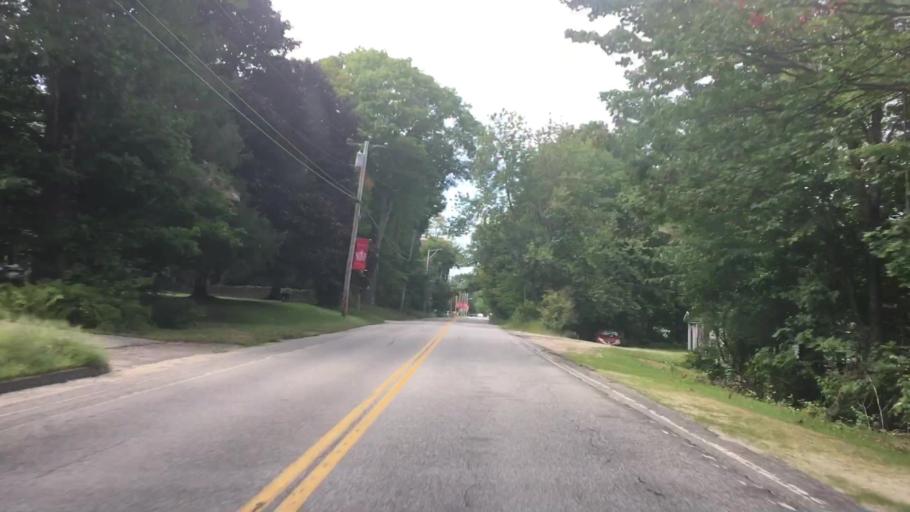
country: US
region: Maine
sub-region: Cumberland County
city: Raymond
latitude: 44.0011
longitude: -70.5200
